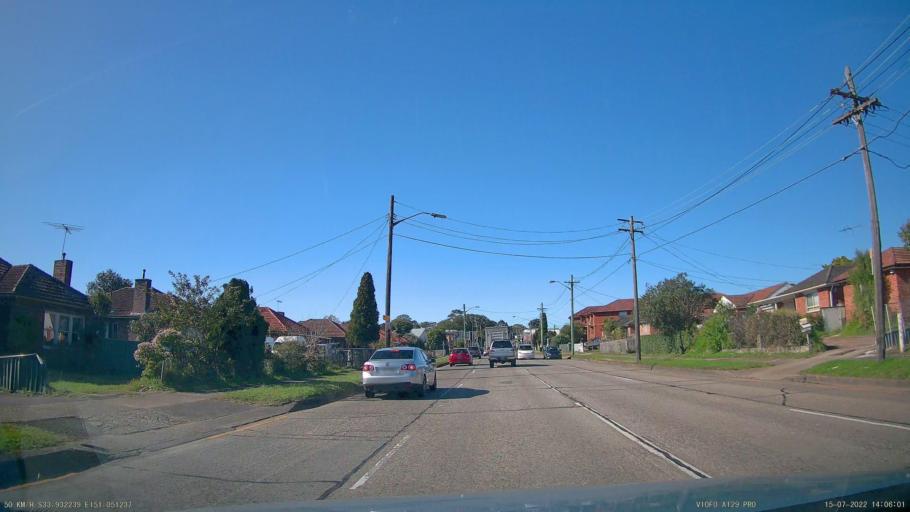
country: AU
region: New South Wales
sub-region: Canterbury
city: Roselands
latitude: -33.9322
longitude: 151.0515
